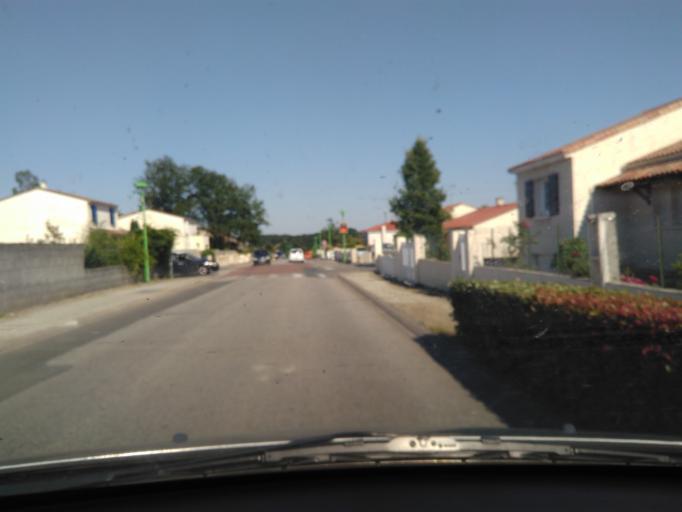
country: FR
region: Pays de la Loire
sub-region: Departement de la Vendee
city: Dompierre-sur-Yon
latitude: 46.7359
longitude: -1.3935
